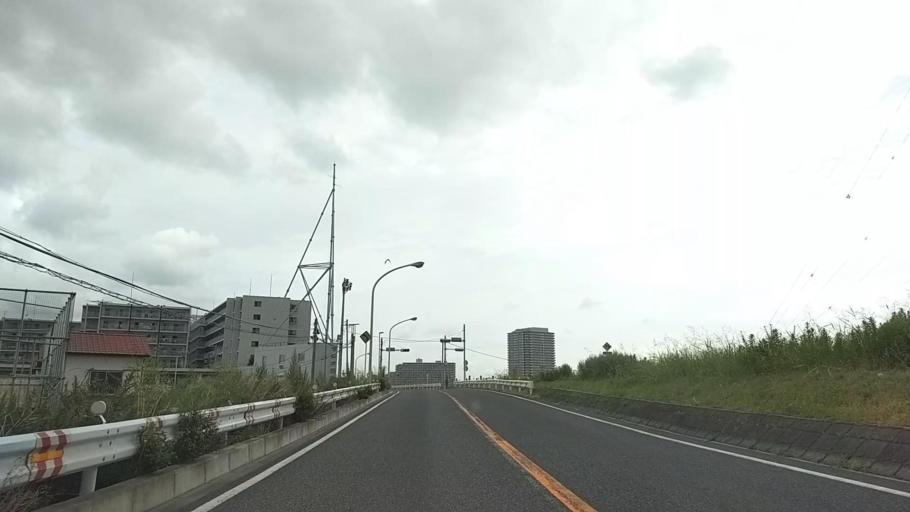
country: JP
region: Kanagawa
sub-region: Kawasaki-shi
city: Kawasaki
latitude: 35.5482
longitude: 139.6983
